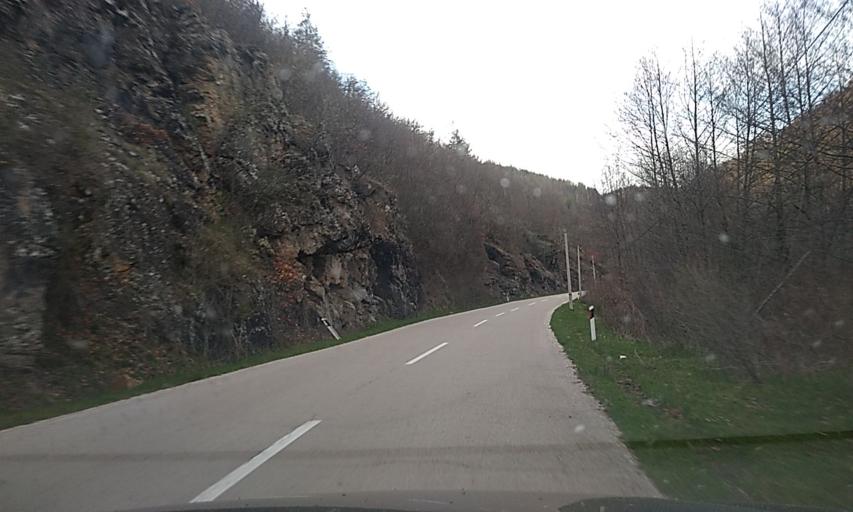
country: RS
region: Central Serbia
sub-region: Pcinjski Okrug
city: Bosilegrad
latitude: 42.4338
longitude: 22.5122
